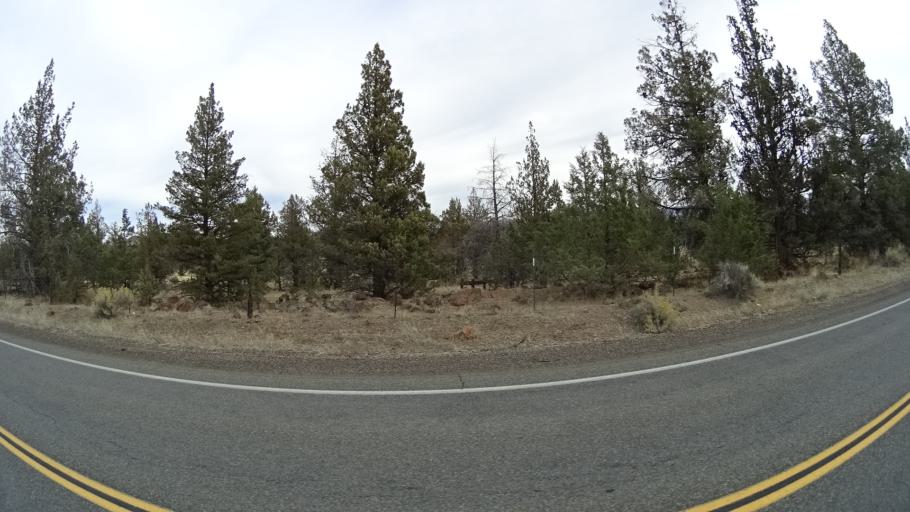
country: US
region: California
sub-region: Siskiyou County
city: Montague
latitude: 41.6367
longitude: -122.4554
